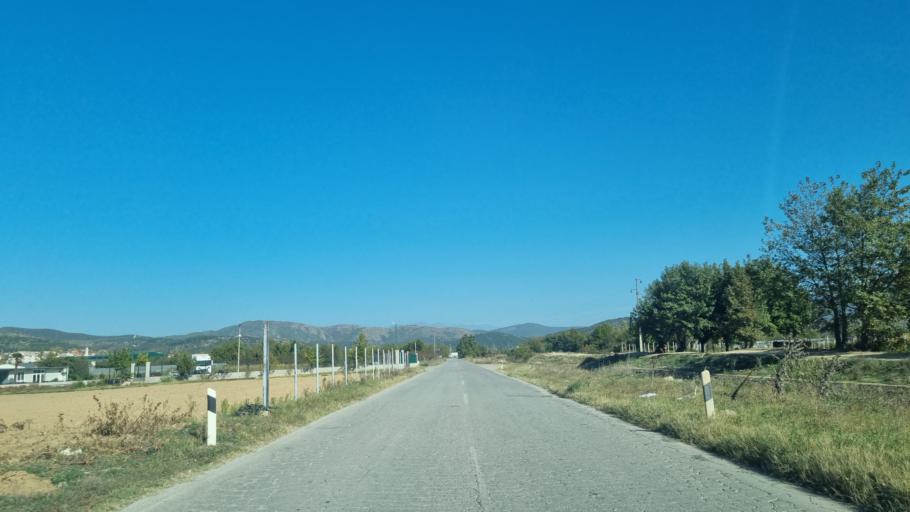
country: MK
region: Bogdanci
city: Bogdanci
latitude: 41.1923
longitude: 22.5673
